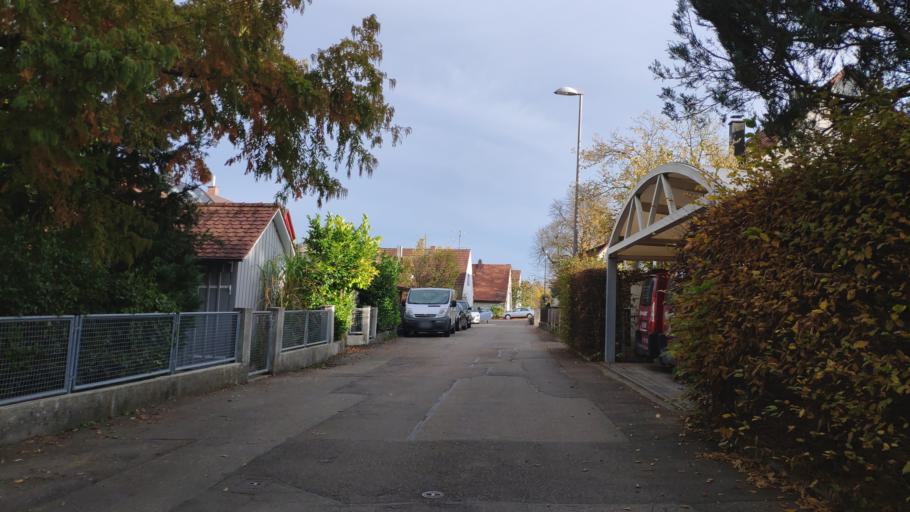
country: DE
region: Baden-Wuerttemberg
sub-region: Tuebingen Region
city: Ulm
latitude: 48.4016
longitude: 9.9392
